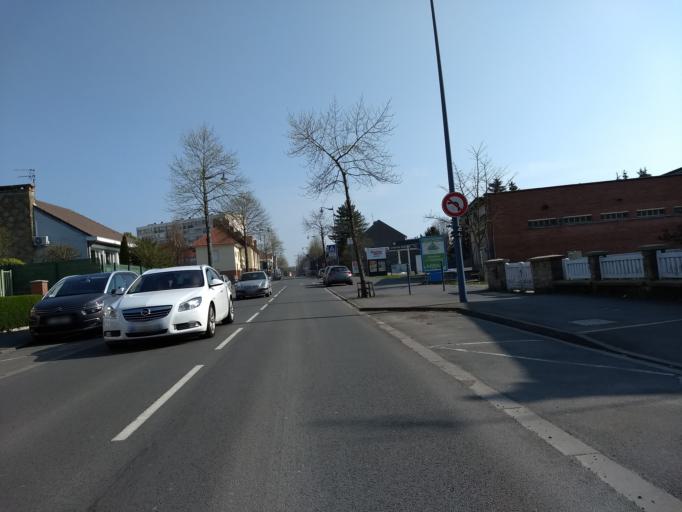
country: FR
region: Nord-Pas-de-Calais
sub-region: Departement du Pas-de-Calais
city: Achicourt
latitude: 50.2891
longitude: 2.7484
